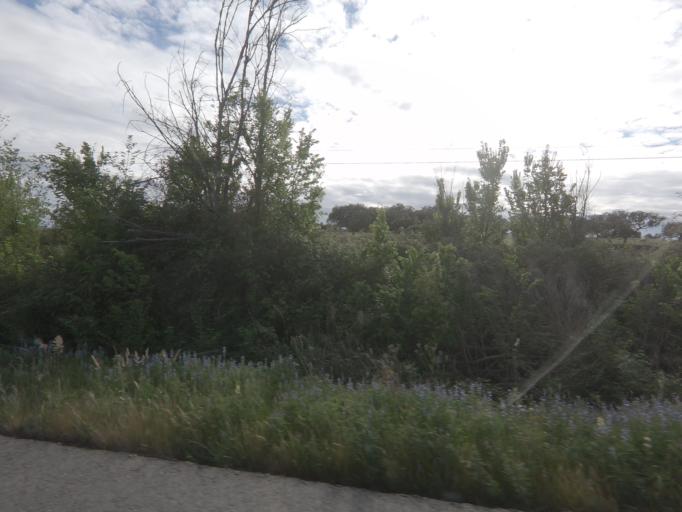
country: ES
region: Extremadura
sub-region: Provincia de Caceres
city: Moraleja
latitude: 40.0934
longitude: -6.6745
